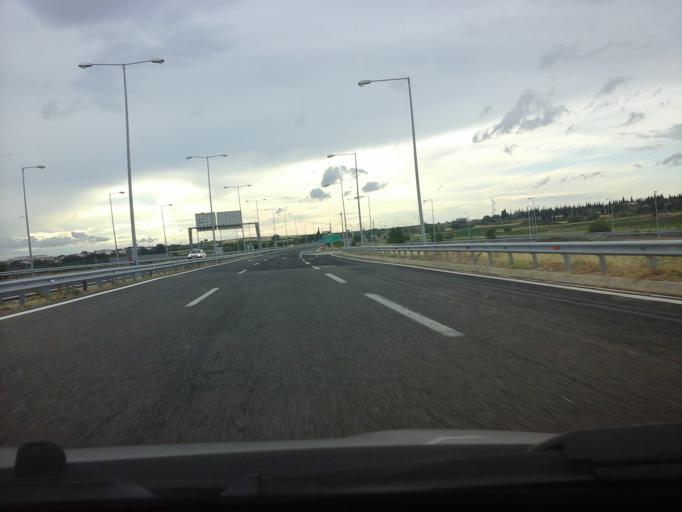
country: GR
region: East Macedonia and Thrace
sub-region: Nomos Rodopis
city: Komotini
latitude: 41.0960
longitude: 25.4341
